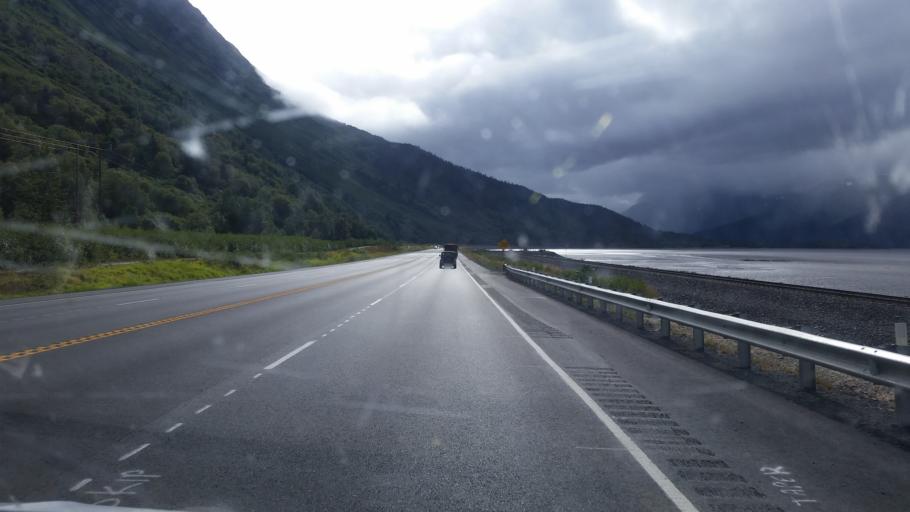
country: US
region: Alaska
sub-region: Anchorage Municipality
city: Girdwood
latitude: 60.9511
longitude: -149.4032
